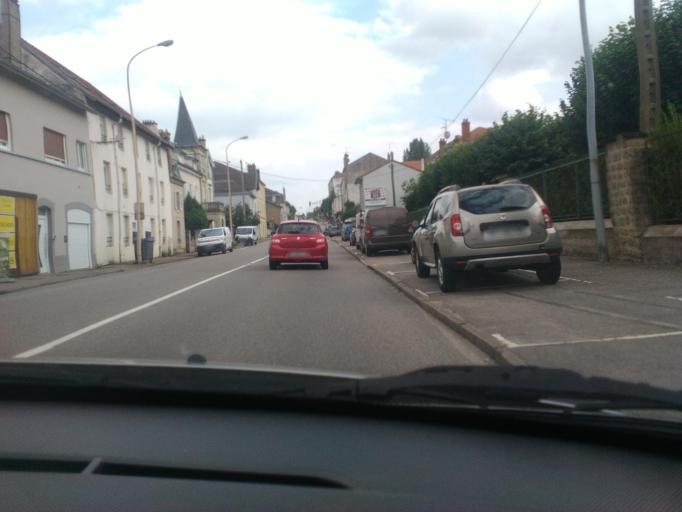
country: FR
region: Lorraine
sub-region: Departement de Meurthe-et-Moselle
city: Frouard
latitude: 48.7562
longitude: 6.1395
